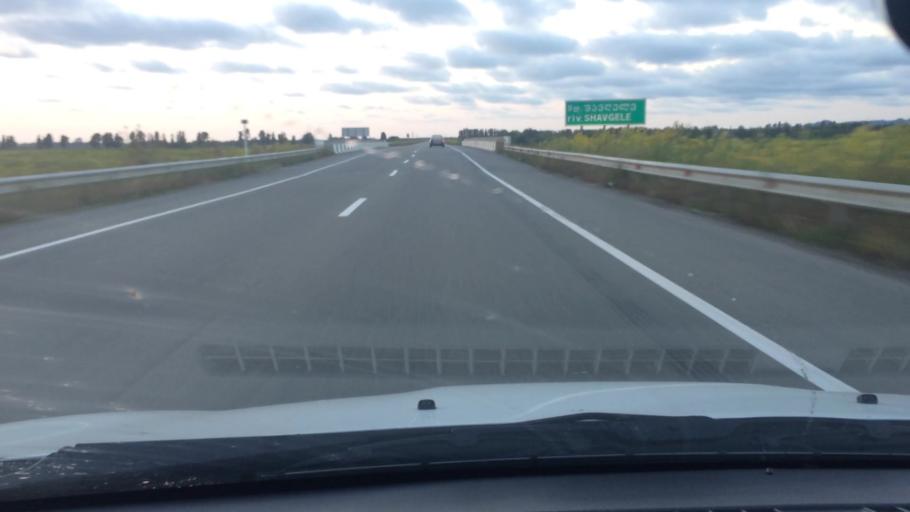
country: GE
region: Ajaria
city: Ochkhamuri
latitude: 41.8775
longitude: 41.8230
